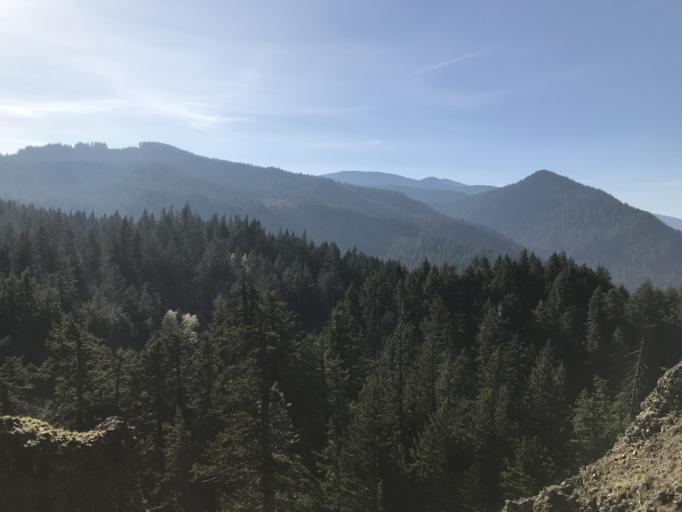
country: US
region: Oregon
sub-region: Hood River County
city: Hood River
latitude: 45.6995
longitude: -121.6143
